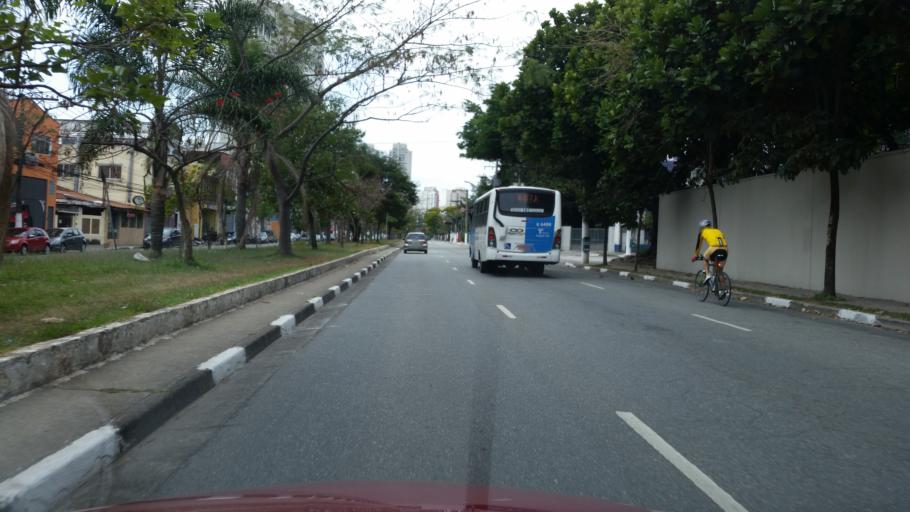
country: BR
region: Sao Paulo
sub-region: Diadema
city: Diadema
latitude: -23.6731
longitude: -46.6971
